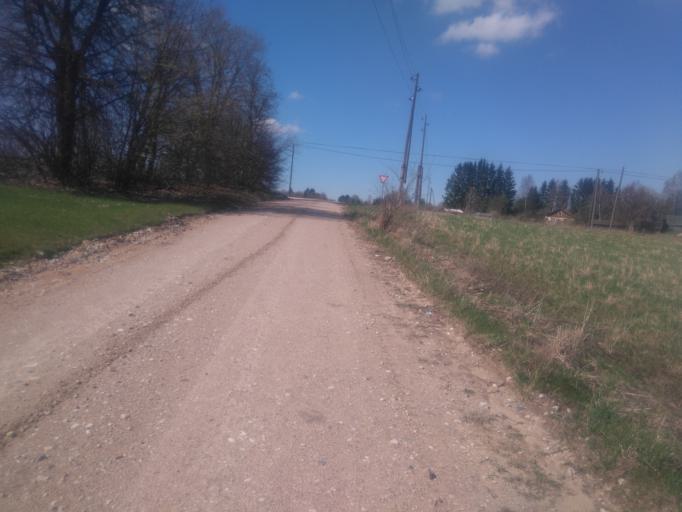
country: LV
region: Vecpiebalga
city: Vecpiebalga
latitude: 57.0222
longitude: 25.8365
